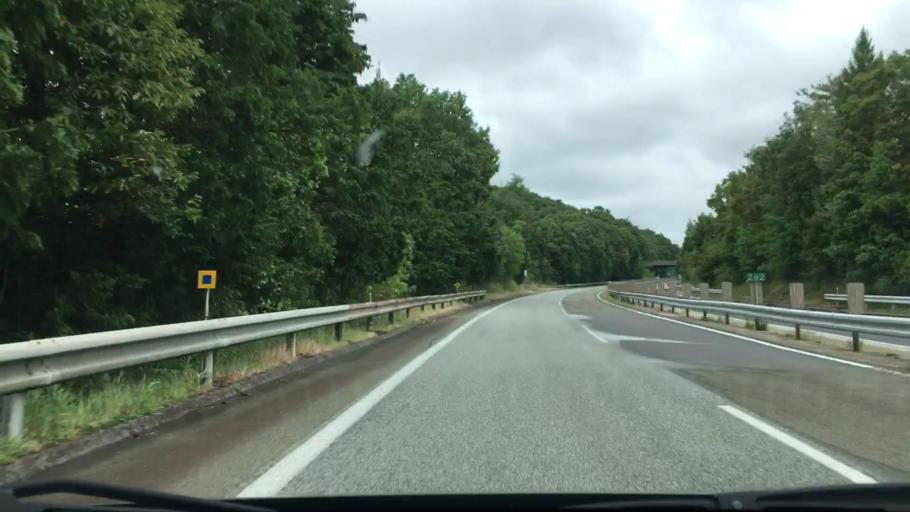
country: JP
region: Hiroshima
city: Miyoshi
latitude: 34.7894
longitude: 132.8793
